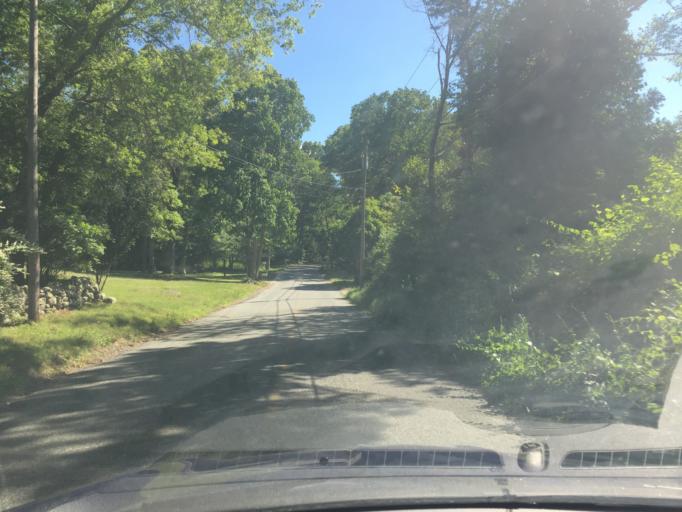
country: US
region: Rhode Island
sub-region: Washington County
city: Hopkinton
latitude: 41.4795
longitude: -71.8098
